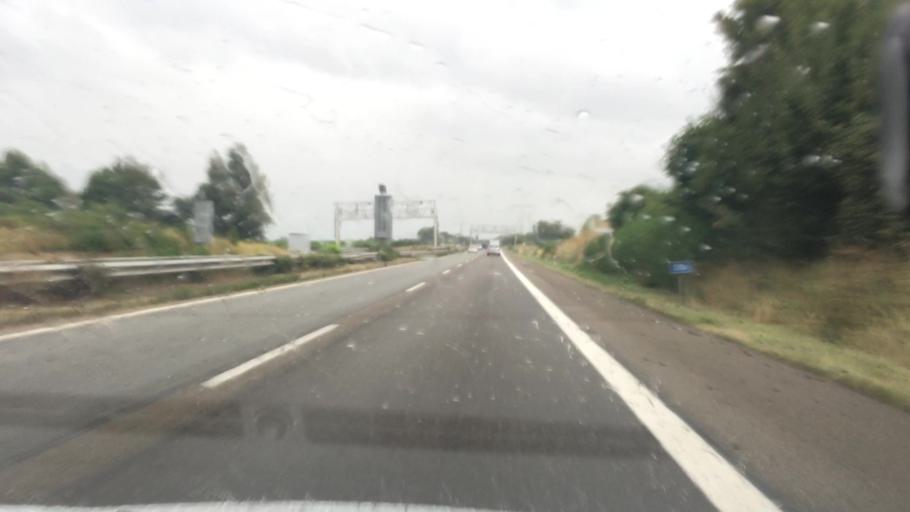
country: DE
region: Rheinland-Pfalz
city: Edesheim
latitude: 49.2623
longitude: 8.1515
